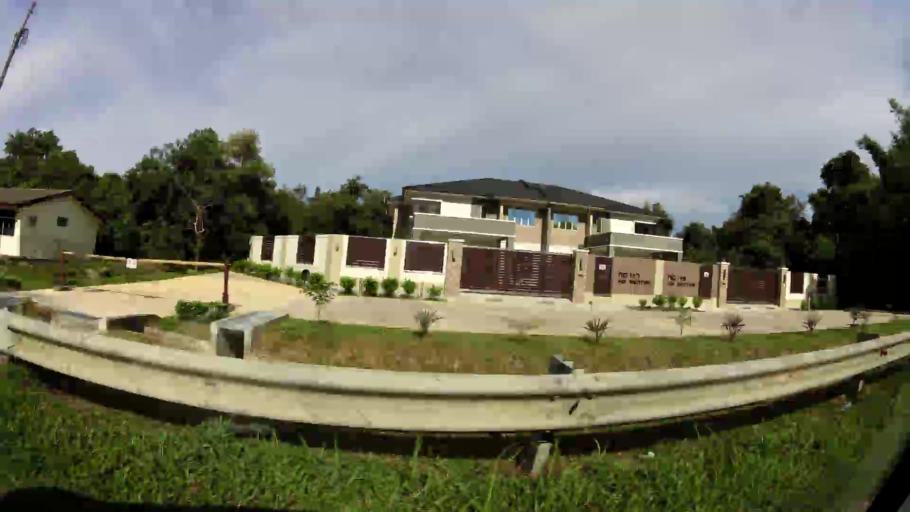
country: BN
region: Brunei and Muara
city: Bandar Seri Begawan
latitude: 4.9834
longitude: 115.0223
